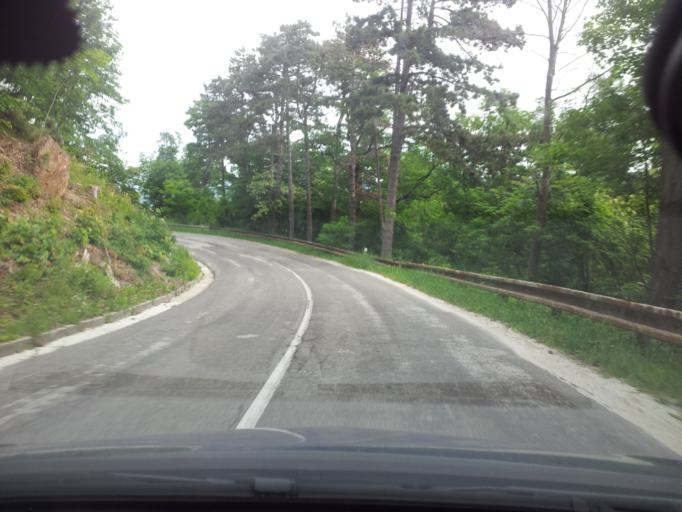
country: SK
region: Nitriansky
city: Partizanske
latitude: 48.5671
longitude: 18.4590
